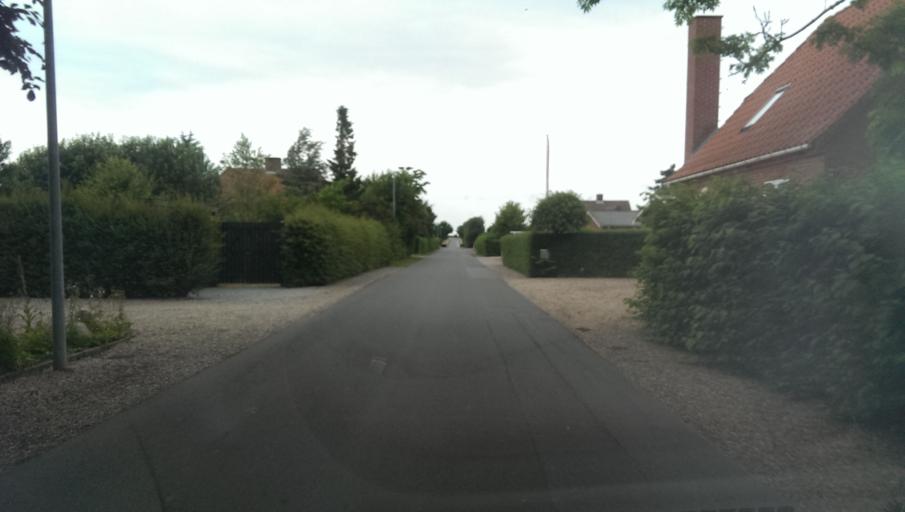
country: DK
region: South Denmark
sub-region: Esbjerg Kommune
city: Bramming
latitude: 55.4319
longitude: 8.6488
